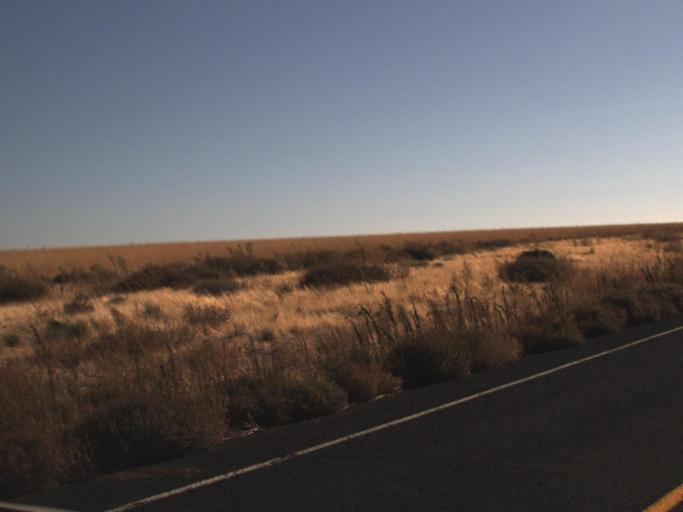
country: US
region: Washington
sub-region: Adams County
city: Ritzville
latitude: 47.0384
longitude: -118.6633
